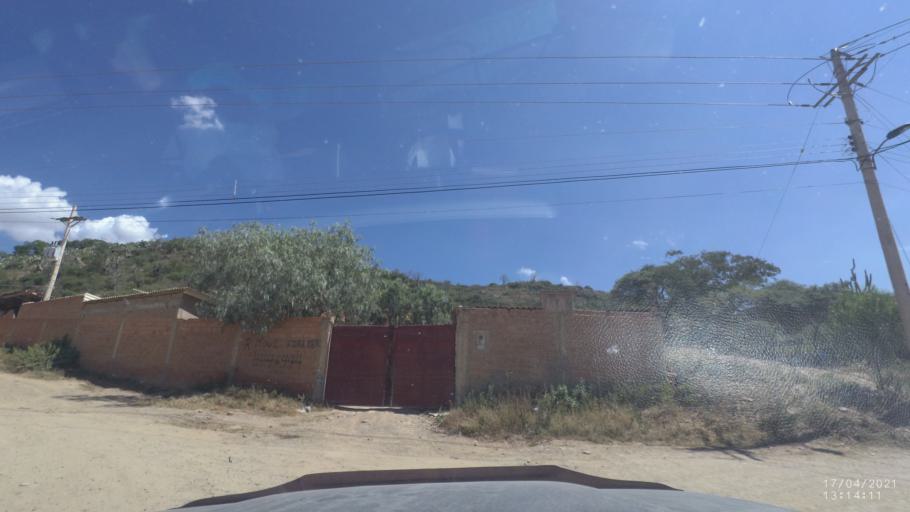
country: BO
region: Cochabamba
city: Cochabamba
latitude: -17.4183
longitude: -66.2251
